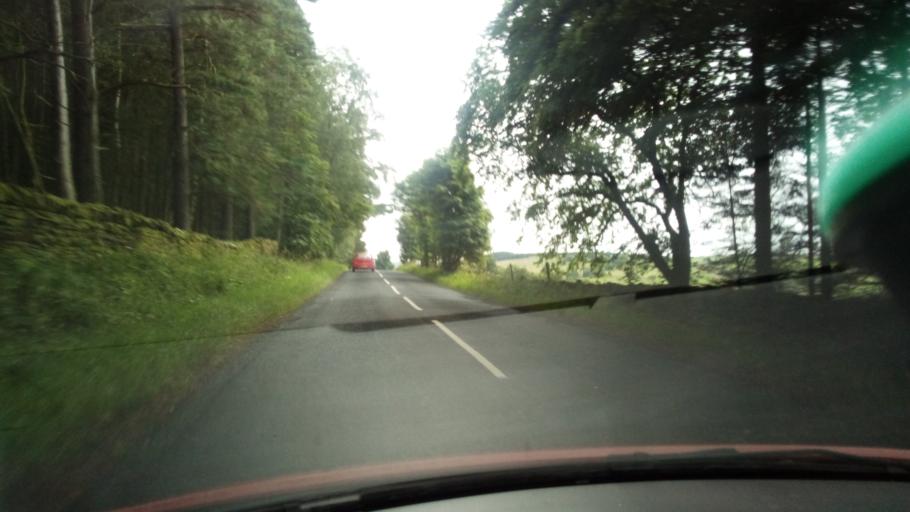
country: GB
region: England
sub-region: Northumberland
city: Slaley
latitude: 54.8573
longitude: -2.0186
